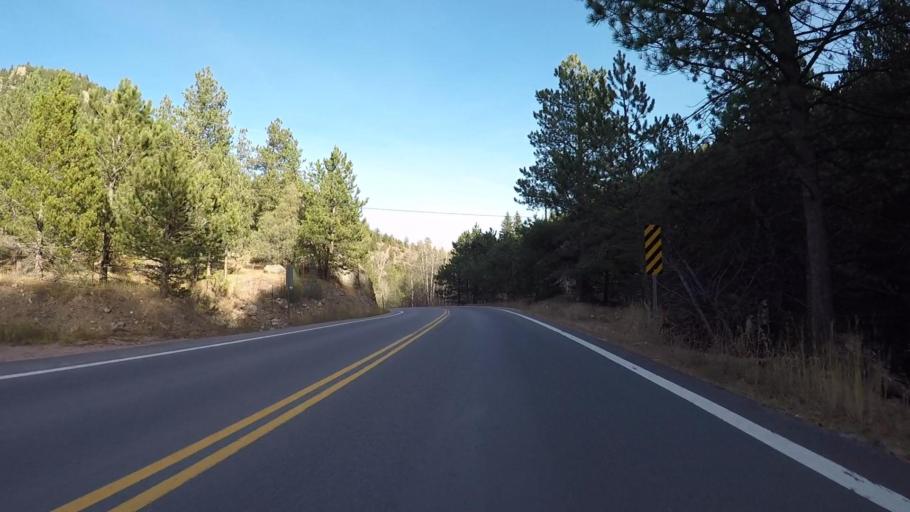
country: US
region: Colorado
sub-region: Boulder County
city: Nederland
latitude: 40.0748
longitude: -105.4174
